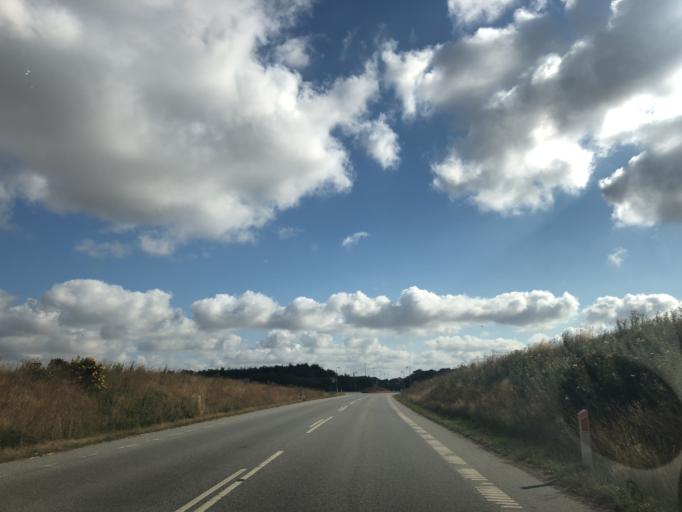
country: DK
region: Central Jutland
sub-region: Skive Kommune
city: Skive
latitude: 56.6431
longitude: 8.9230
